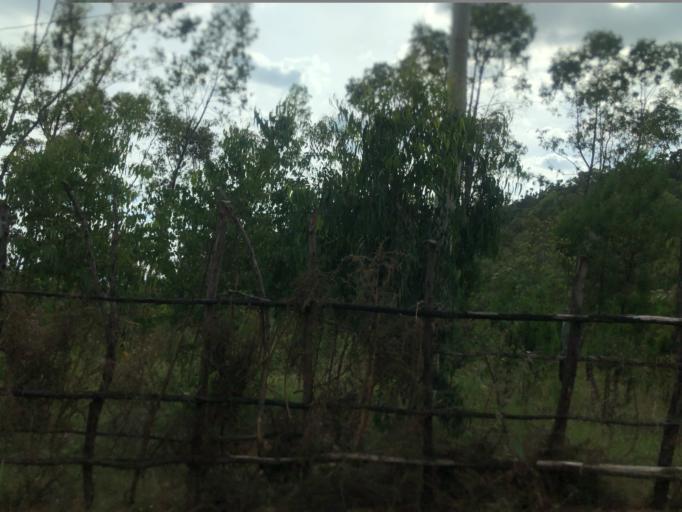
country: ET
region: Southern Nations, Nationalities, and People's Region
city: Konso
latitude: 5.2776
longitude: 37.3438
